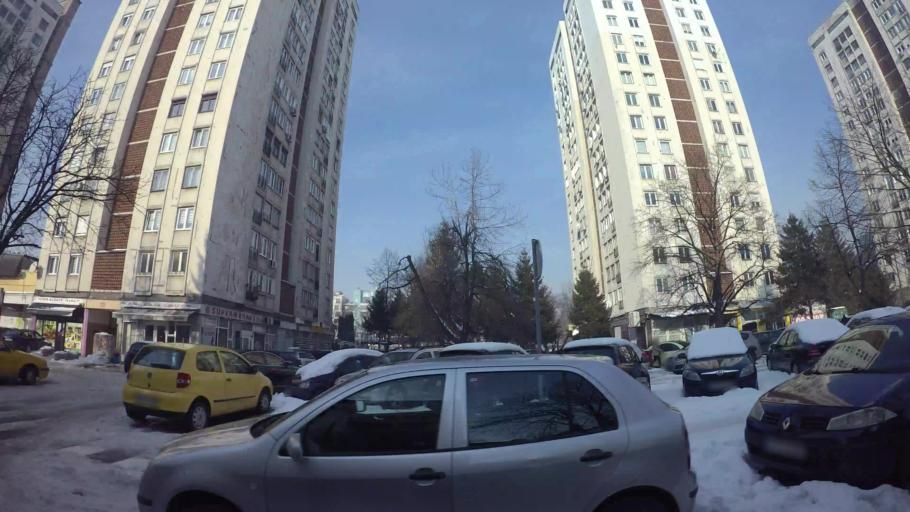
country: BA
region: Federation of Bosnia and Herzegovina
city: Kobilja Glava
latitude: 43.8526
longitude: 18.4005
